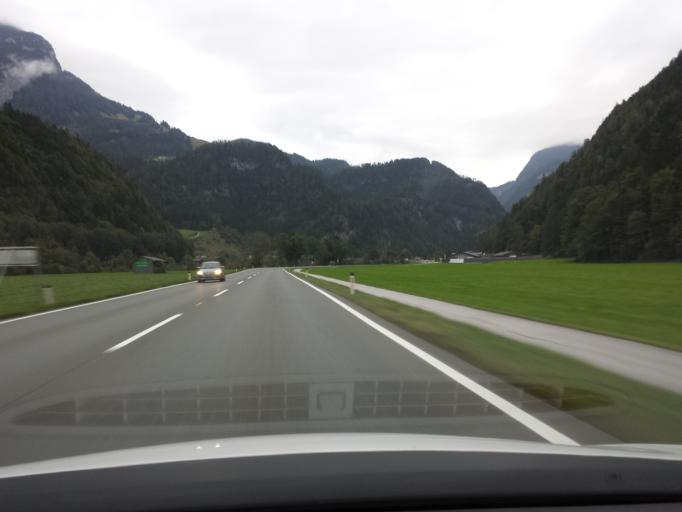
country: AT
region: Salzburg
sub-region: Politischer Bezirk Zell am See
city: Sankt Martin bei Lofer
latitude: 47.5258
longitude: 12.7423
